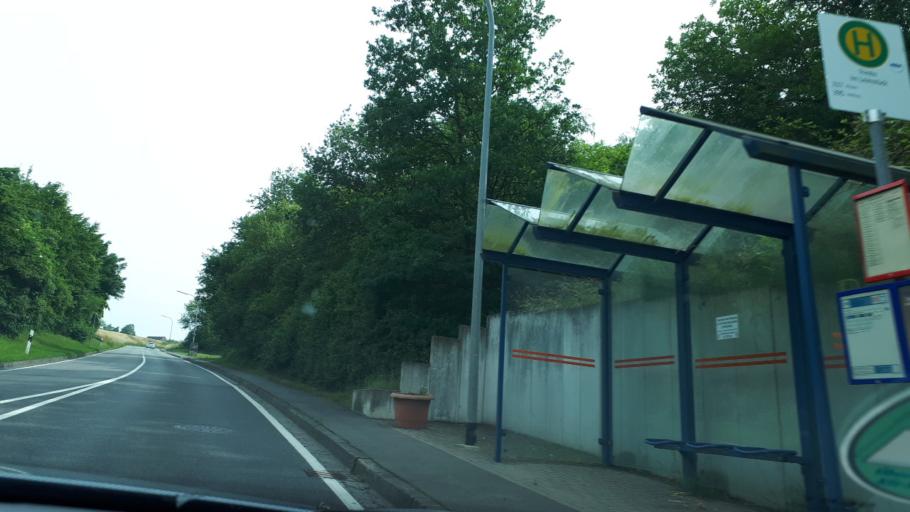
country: DE
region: Rheinland-Pfalz
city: Trimbs
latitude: 50.3286
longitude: 7.3027
